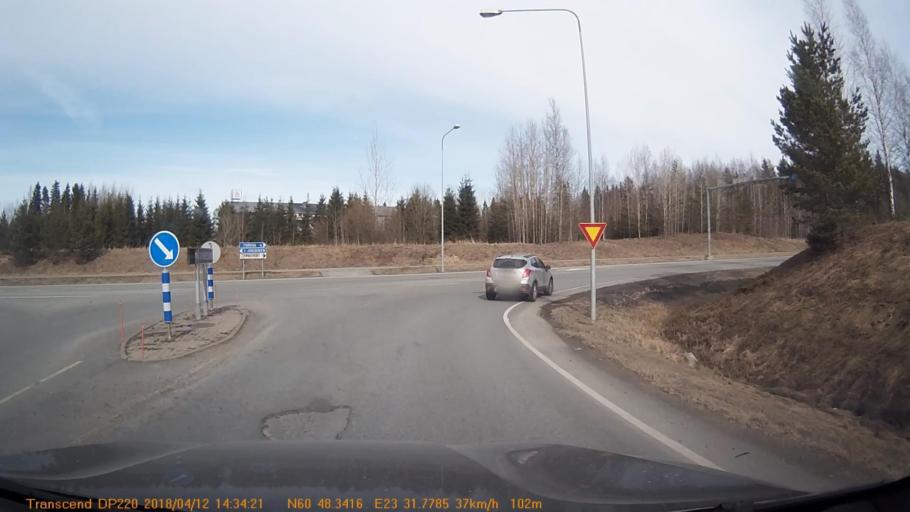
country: FI
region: Haeme
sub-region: Forssa
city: Jokioinen
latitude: 60.8058
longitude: 23.5298
